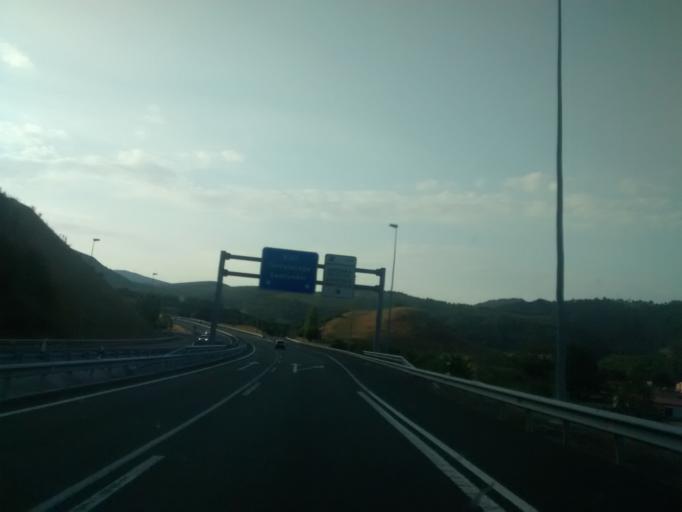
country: ES
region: Cantabria
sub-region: Provincia de Cantabria
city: Arenas de Iguna
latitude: 43.1806
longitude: -4.0570
